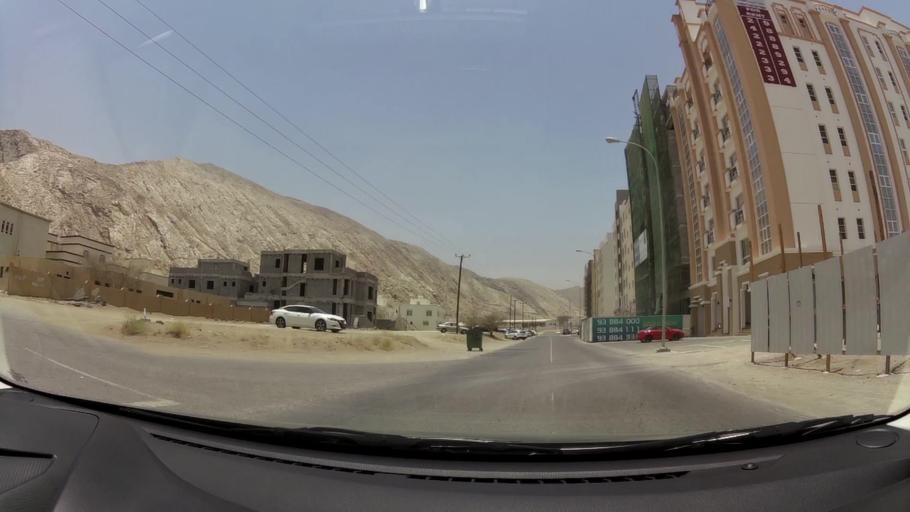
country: OM
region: Muhafazat Masqat
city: Bawshar
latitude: 23.5639
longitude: 58.4203
